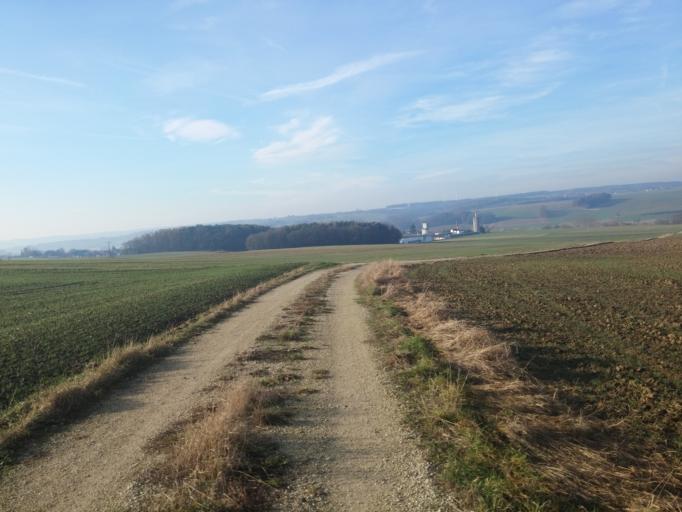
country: DE
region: Bavaria
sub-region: Upper Franconia
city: Grossheirath
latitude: 50.1667
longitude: 10.9530
